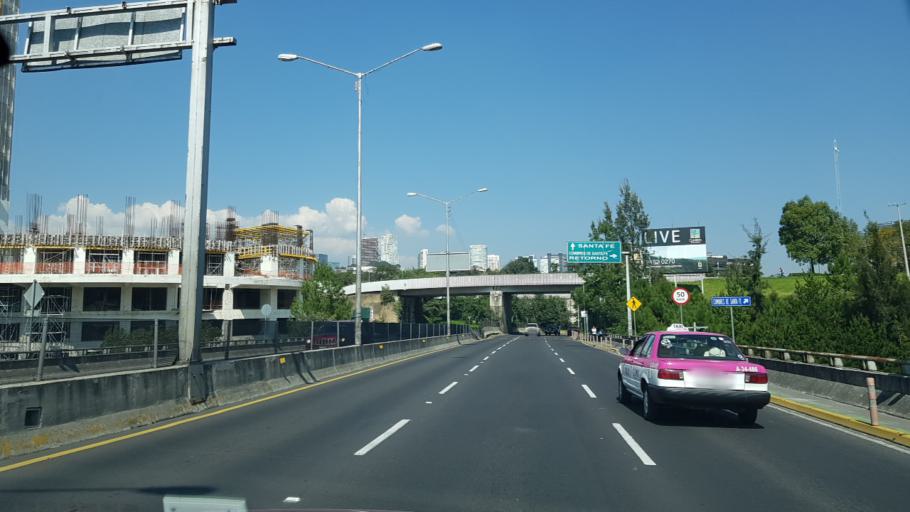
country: MX
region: Mexico City
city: Col. Bosques de las Lomas
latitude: 19.3483
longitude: -99.2585
